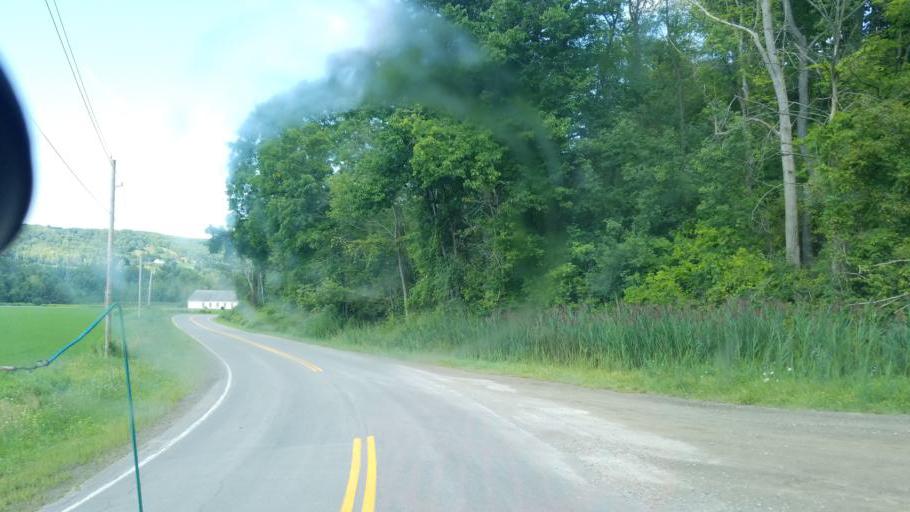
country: US
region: New York
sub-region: Steuben County
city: Canisteo
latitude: 42.2932
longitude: -77.6178
